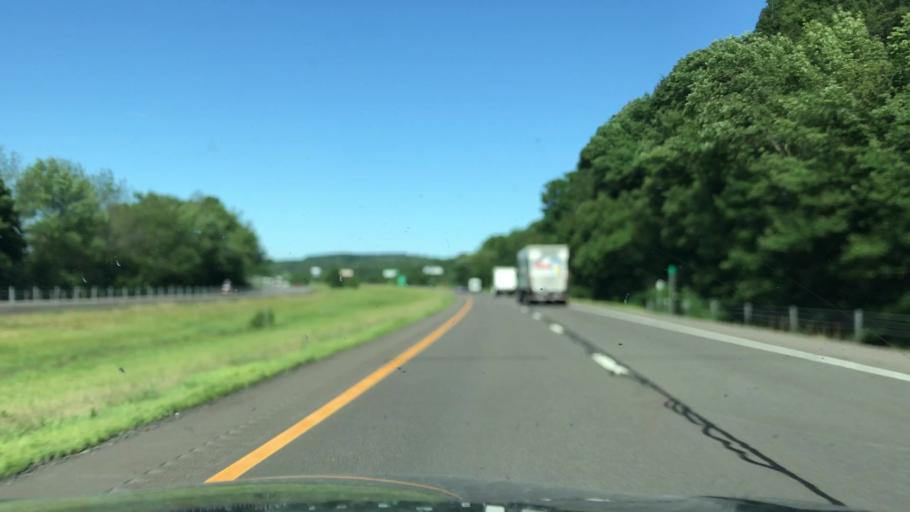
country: US
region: New York
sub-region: Tioga County
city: Owego
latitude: 42.0830
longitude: -76.2889
